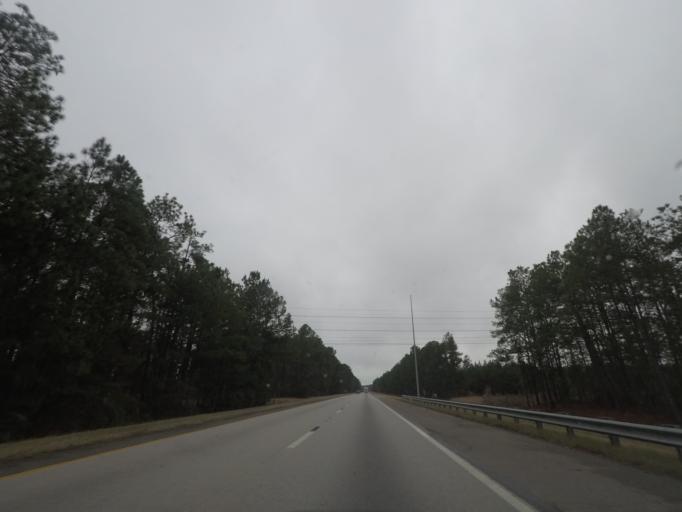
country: US
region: South Carolina
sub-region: Dorchester County
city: Saint George
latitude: 33.0610
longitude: -80.6638
